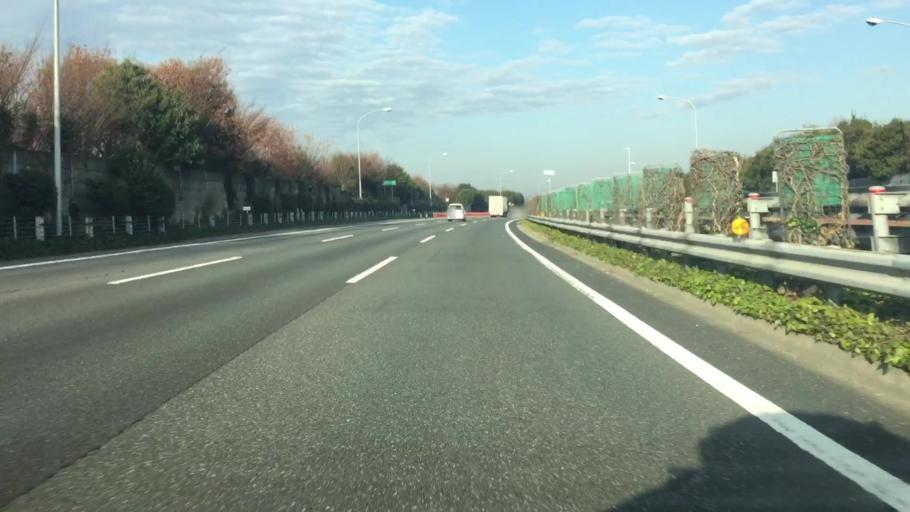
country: JP
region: Saitama
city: Ogawa
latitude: 36.0463
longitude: 139.3481
